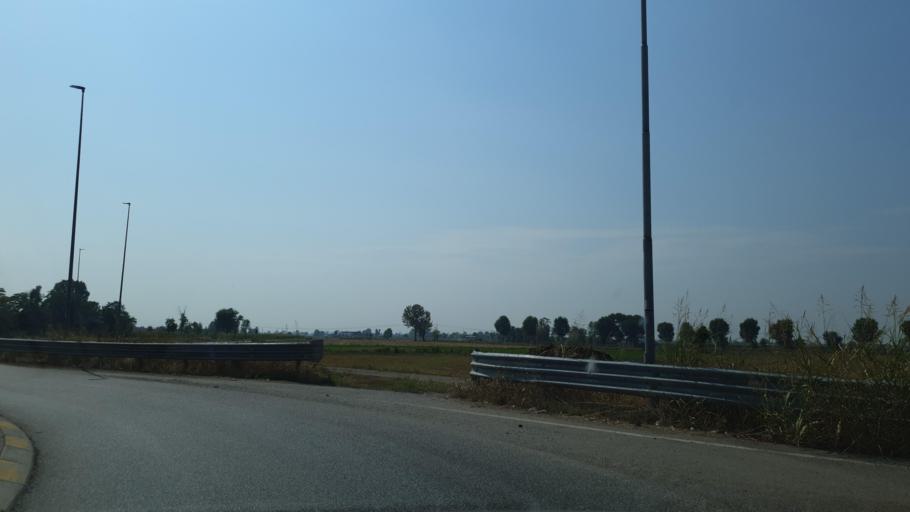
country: IT
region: Lombardy
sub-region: Provincia di Brescia
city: Ghedi
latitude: 45.4095
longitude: 10.2564
